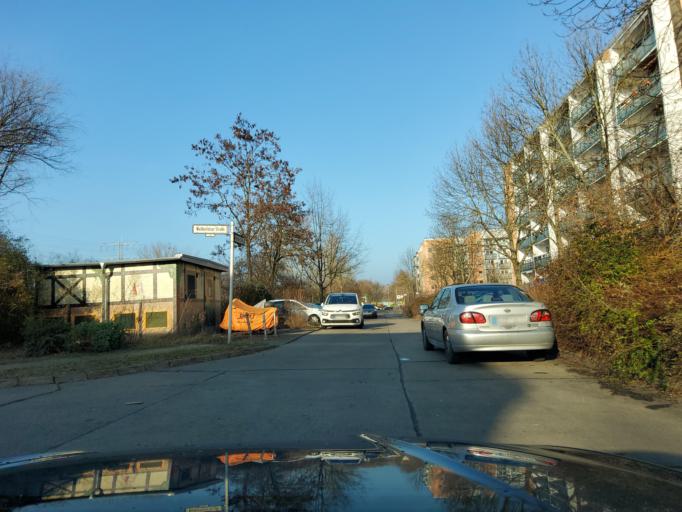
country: DE
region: Berlin
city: Hellersdorf
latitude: 52.5394
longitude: 13.6150
